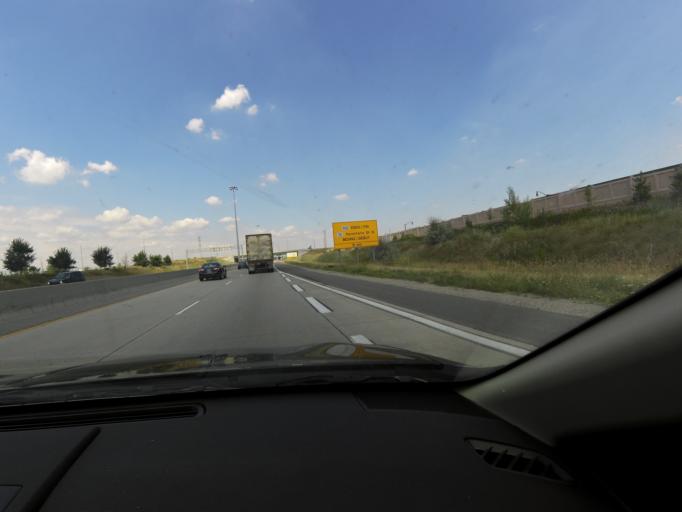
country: CA
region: Ontario
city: Brampton
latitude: 43.7454
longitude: -79.7862
